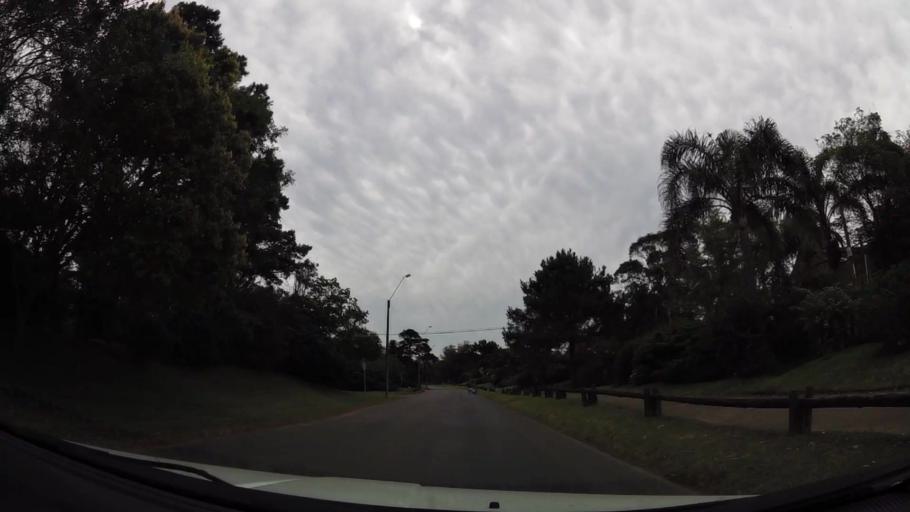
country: UY
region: Maldonado
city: Maldonado
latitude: -34.9071
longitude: -54.9968
